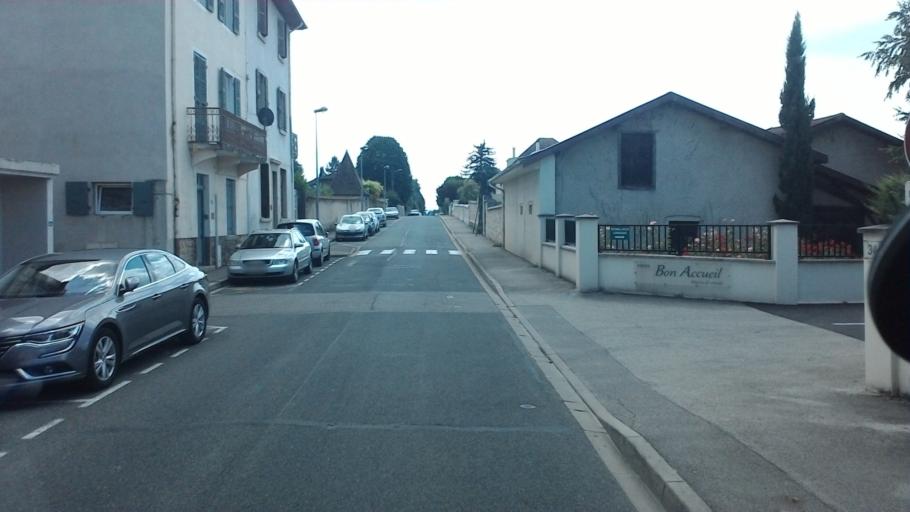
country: FR
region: Rhone-Alpes
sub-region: Departement de l'Ain
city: Lagnieu
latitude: 45.9018
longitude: 5.3505
